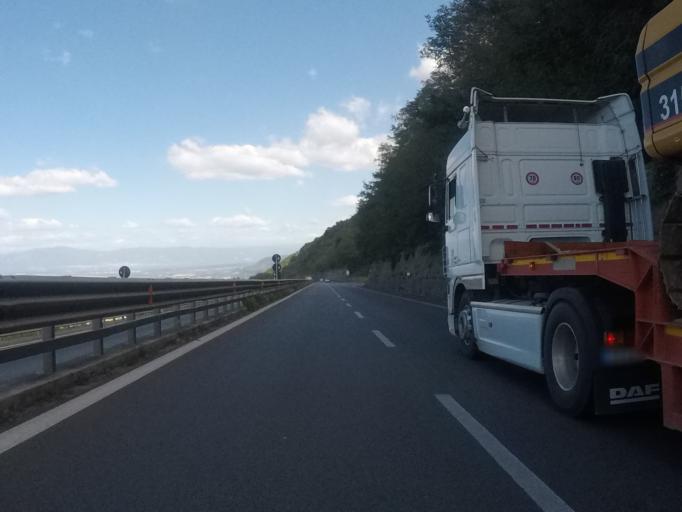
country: IT
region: Calabria
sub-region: Provincia di Vibo-Valentia
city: Maierato
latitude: 38.7197
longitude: 16.1563
